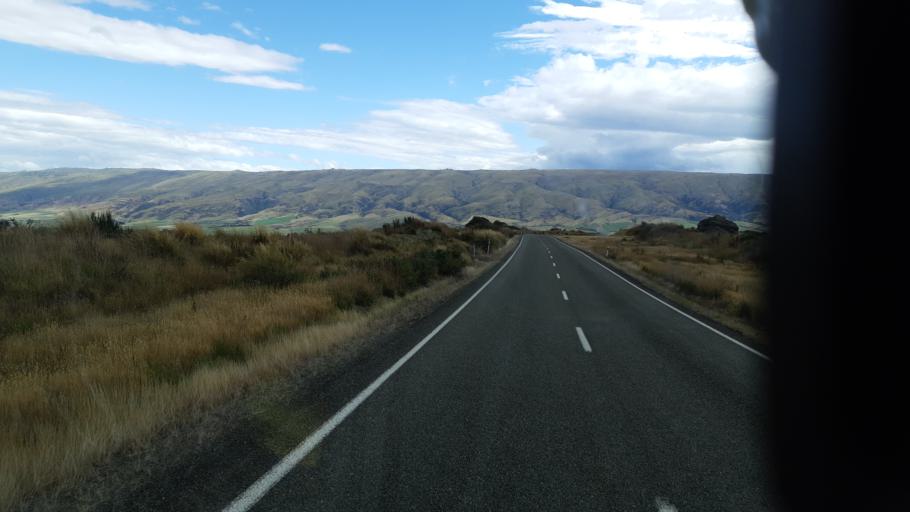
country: NZ
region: Otago
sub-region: Dunedin City
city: Dunedin
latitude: -45.3603
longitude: 170.3189
